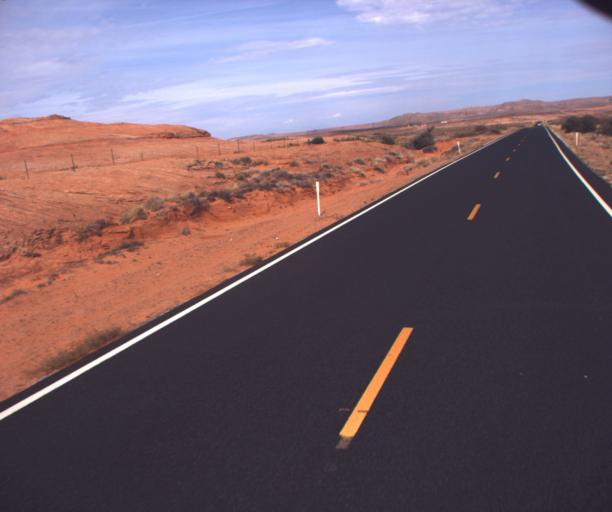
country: US
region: Arizona
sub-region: Apache County
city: Many Farms
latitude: 36.9145
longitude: -109.6220
